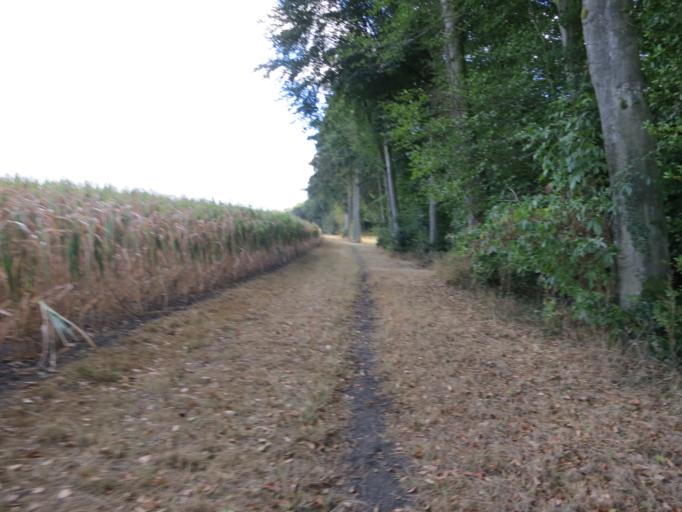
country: DE
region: North Rhine-Westphalia
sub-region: Regierungsbezirk Munster
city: Birgte
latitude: 52.2373
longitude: 7.6338
